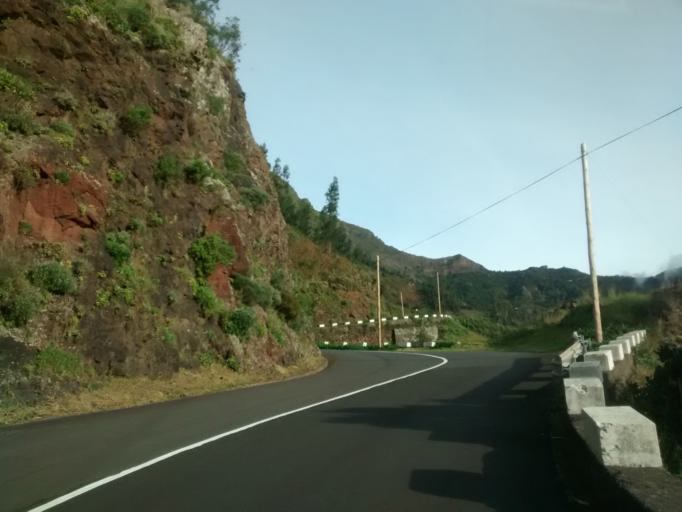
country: PT
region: Madeira
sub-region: Camara de Lobos
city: Curral das Freiras
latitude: 32.7381
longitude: -17.0247
